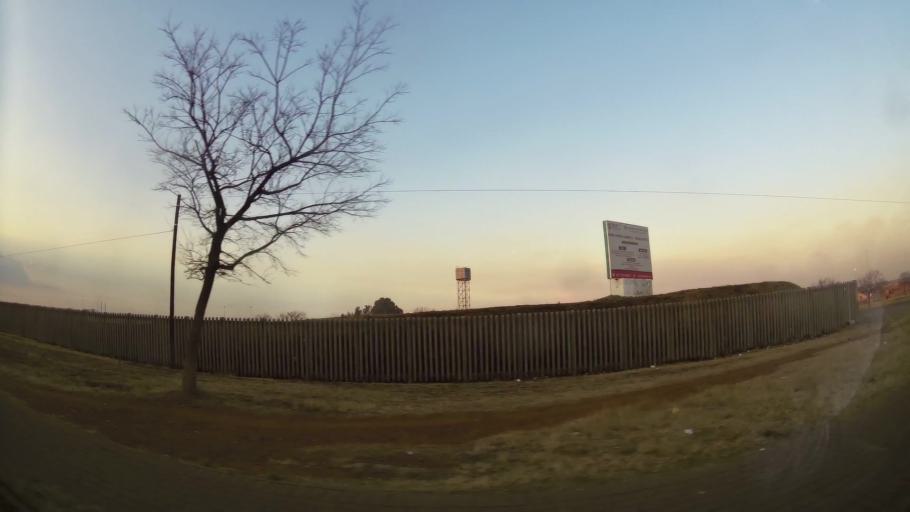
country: ZA
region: Gauteng
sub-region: Ekurhuleni Metropolitan Municipality
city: Springs
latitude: -26.2890
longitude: 28.4058
